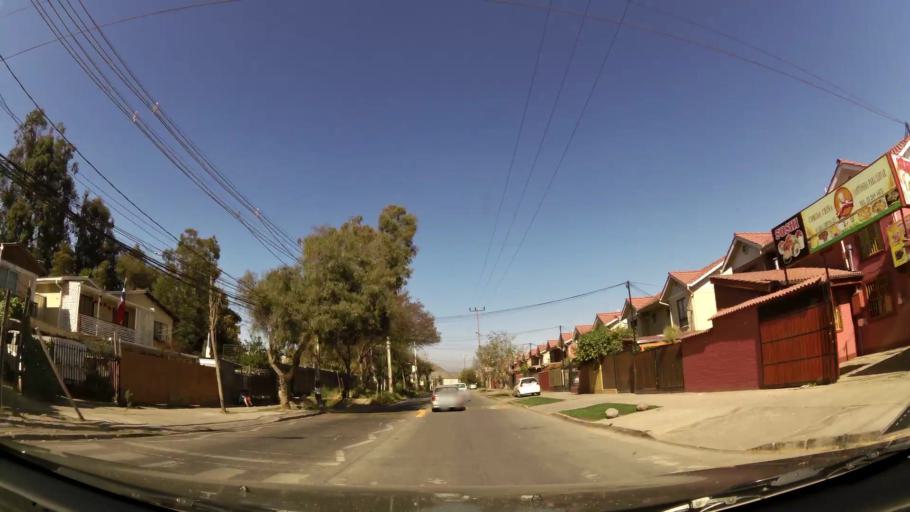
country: CL
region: Santiago Metropolitan
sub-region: Provincia de Maipo
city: San Bernardo
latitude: -33.6150
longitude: -70.7087
